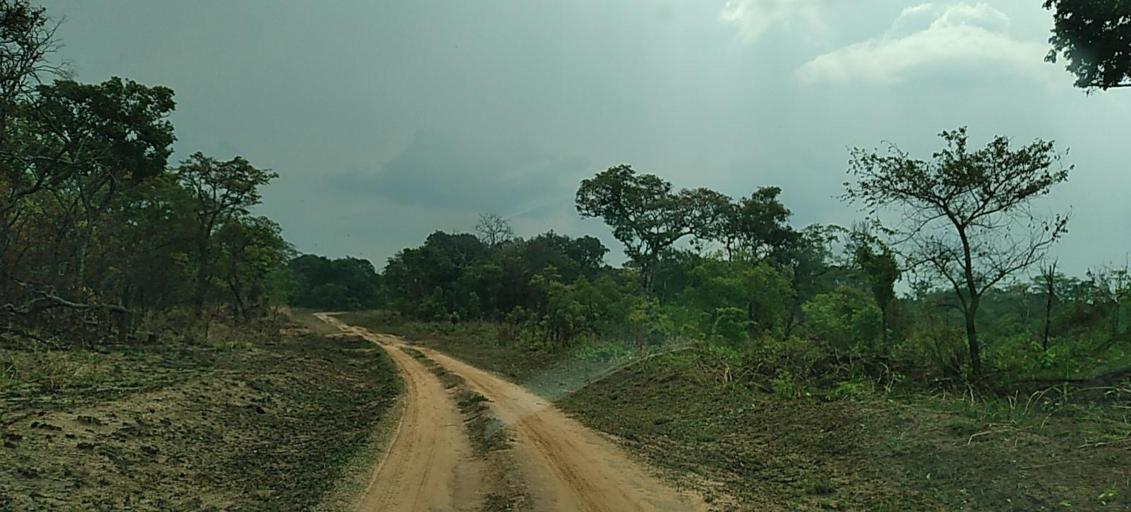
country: ZM
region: North-Western
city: Mwinilunga
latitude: -11.4663
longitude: 24.4772
